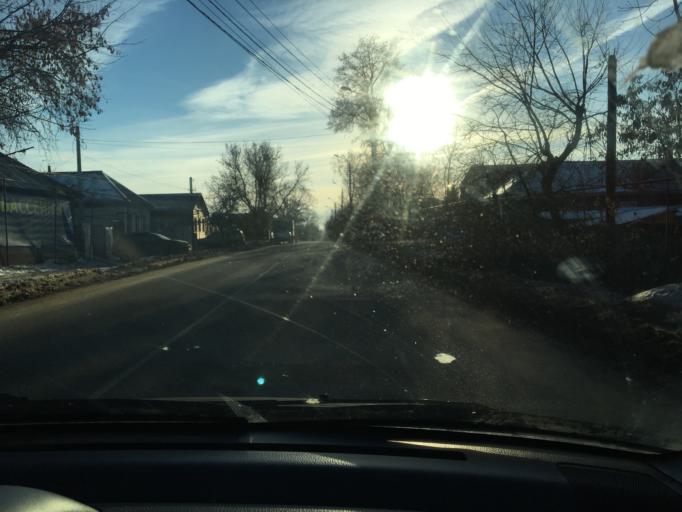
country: RU
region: Tula
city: Tula
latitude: 54.2197
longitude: 37.5979
